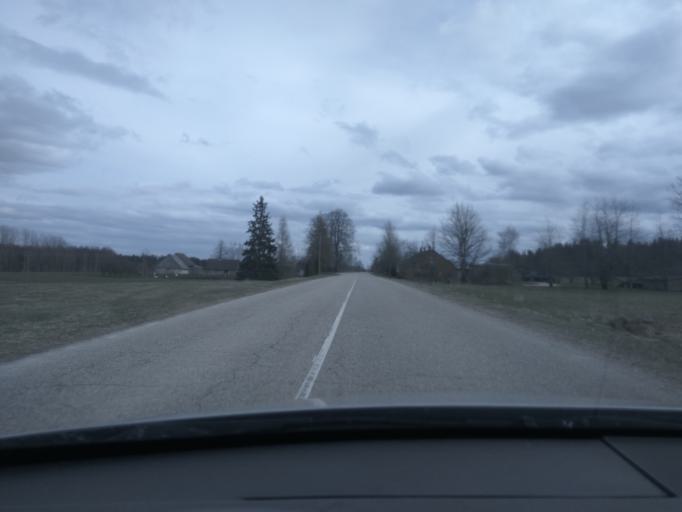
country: LV
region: Aizpute
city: Aizpute
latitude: 56.7749
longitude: 21.5219
